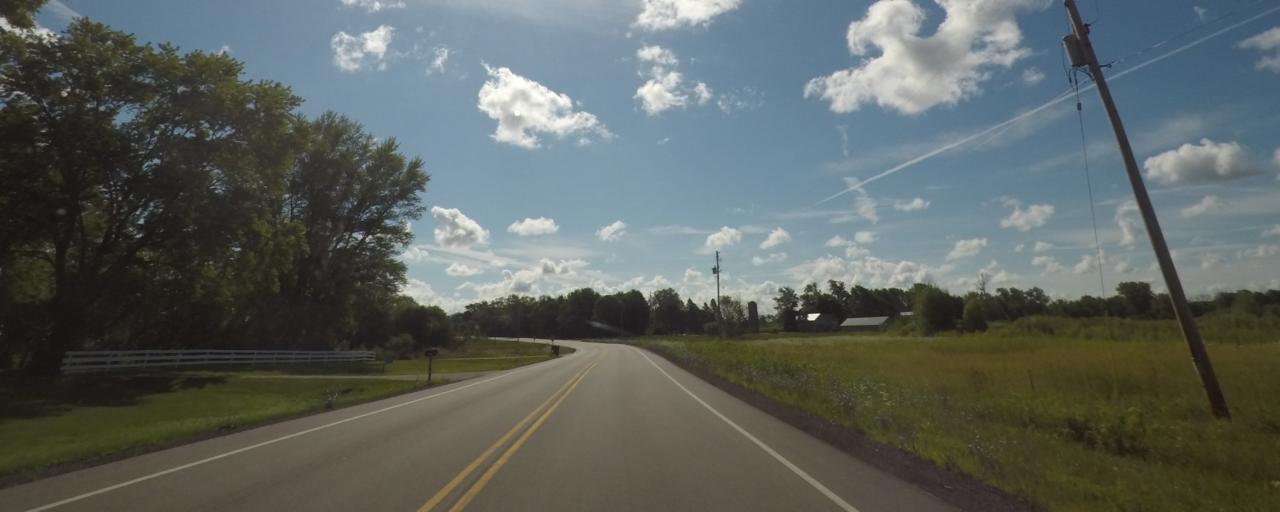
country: US
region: Wisconsin
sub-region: Waukesha County
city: Oconomowoc
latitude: 43.0757
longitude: -88.5579
